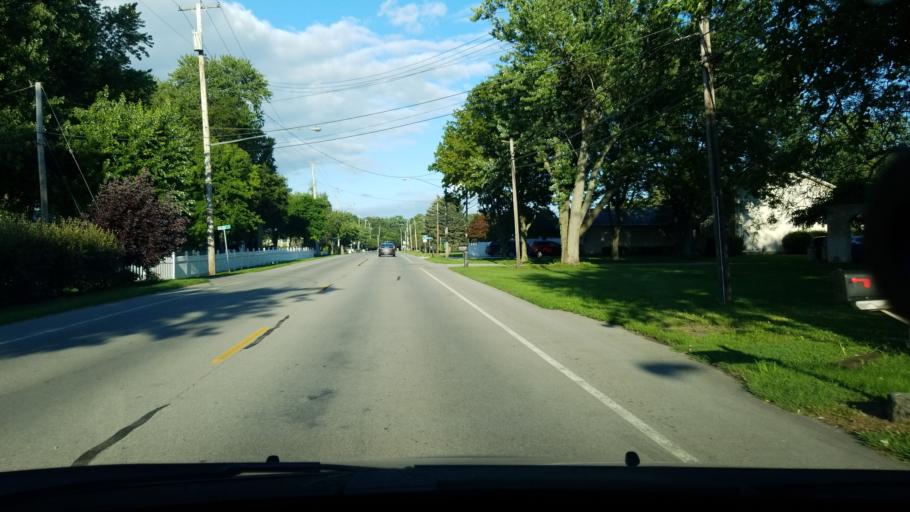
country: US
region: Ohio
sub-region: Erie County
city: Huron
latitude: 41.4077
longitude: -82.5771
